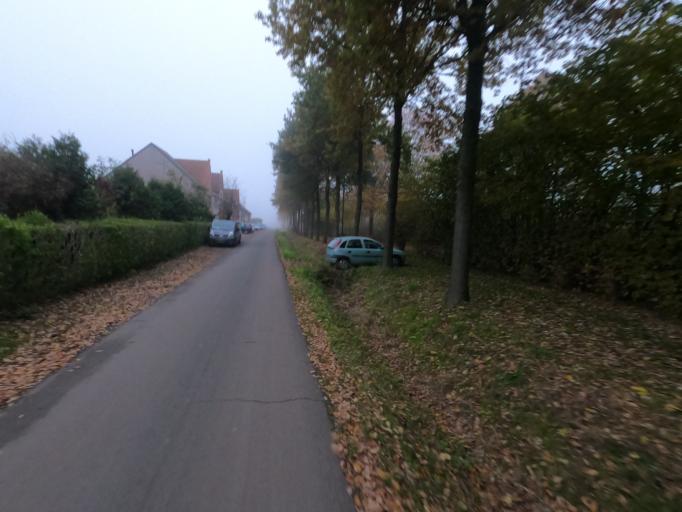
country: BE
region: Flanders
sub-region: Provincie Oost-Vlaanderen
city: Kruibeke
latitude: 51.1898
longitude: 4.3140
